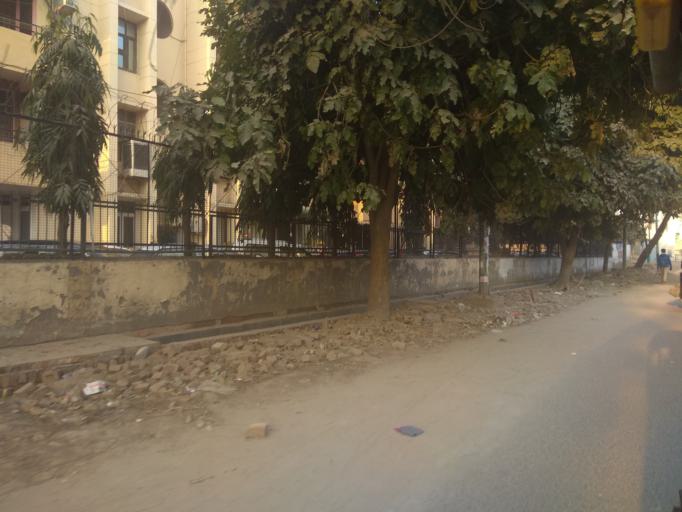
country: IN
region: NCT
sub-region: West Delhi
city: Nangloi Jat
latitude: 28.6353
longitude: 77.0637
